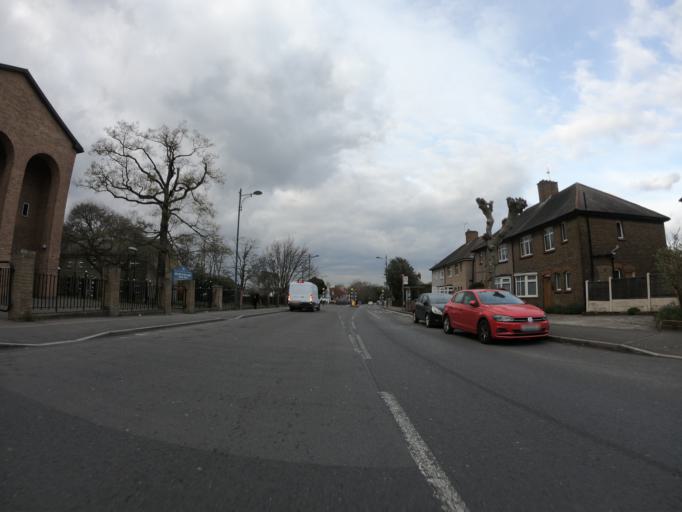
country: GB
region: England
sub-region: Greater London
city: Erith
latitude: 51.4772
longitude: 0.1633
